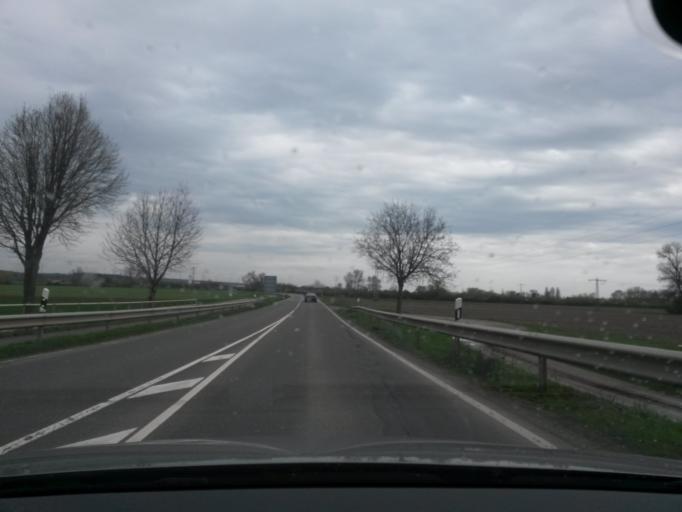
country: DE
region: Rheinland-Pfalz
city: Osthofen
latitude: 49.6788
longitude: 8.3289
